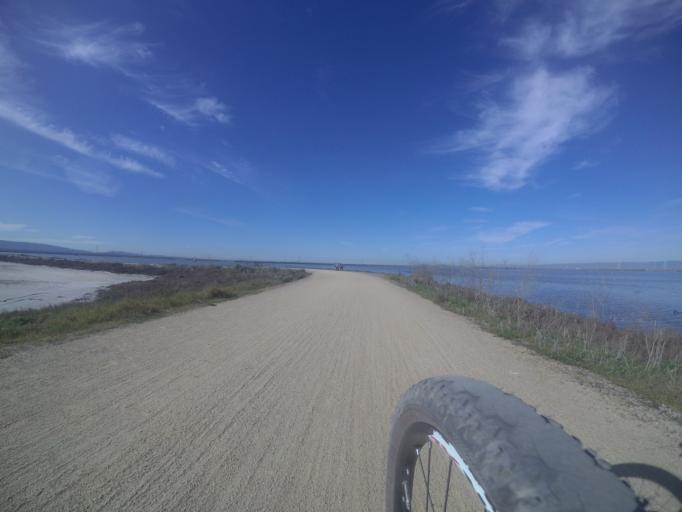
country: US
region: California
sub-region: Santa Clara County
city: Mountain View
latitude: 37.4356
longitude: -122.0540
